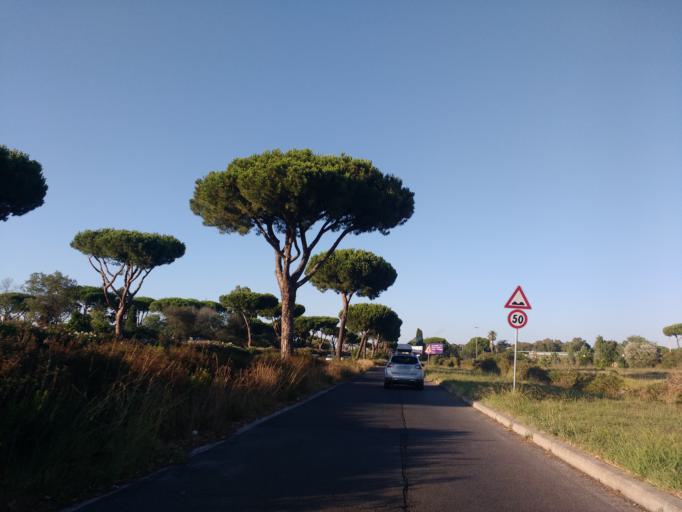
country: IT
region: Latium
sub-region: Citta metropolitana di Roma Capitale
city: Acilia-Castel Fusano-Ostia Antica
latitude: 41.7553
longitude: 12.3706
